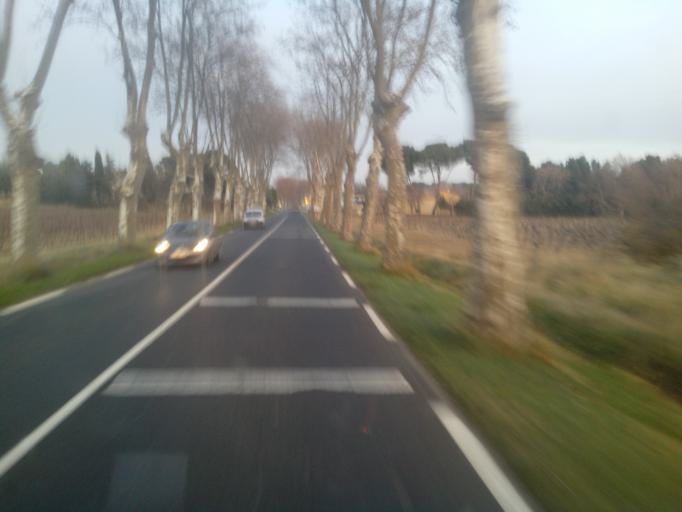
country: FR
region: Languedoc-Roussillon
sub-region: Departement de l'Aude
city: Ginestas
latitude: 43.2831
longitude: 2.8227
